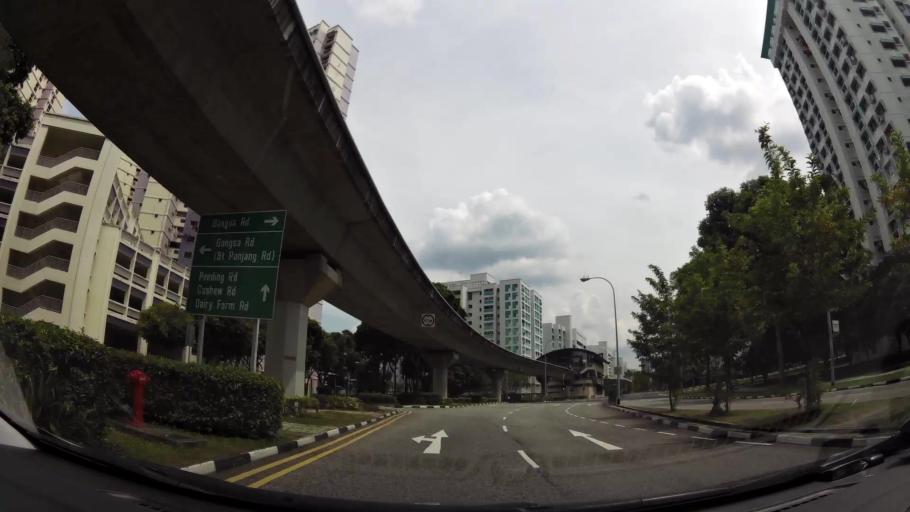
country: MY
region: Johor
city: Johor Bahru
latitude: 1.3782
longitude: 103.7653
